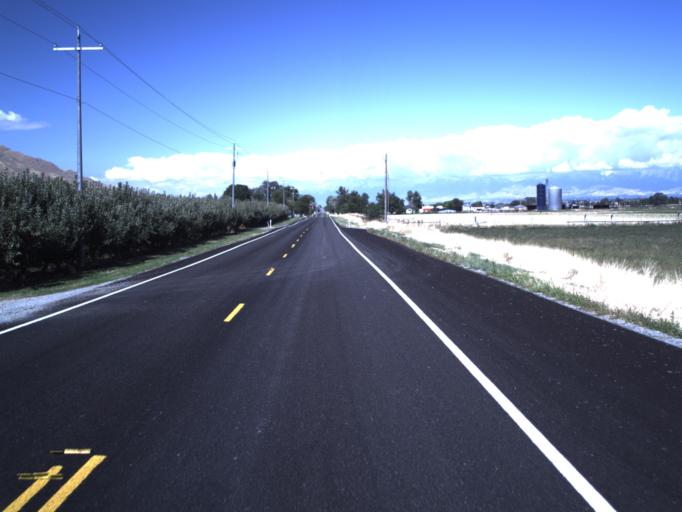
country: US
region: Utah
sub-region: Utah County
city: West Mountain
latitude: 40.0254
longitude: -111.7871
